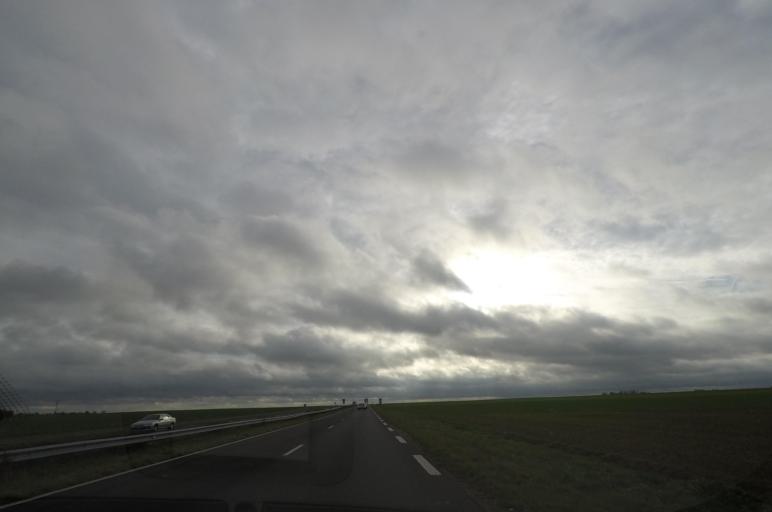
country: FR
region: Centre
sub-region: Departement du Loir-et-Cher
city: Herbault
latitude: 47.7149
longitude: 1.1598
